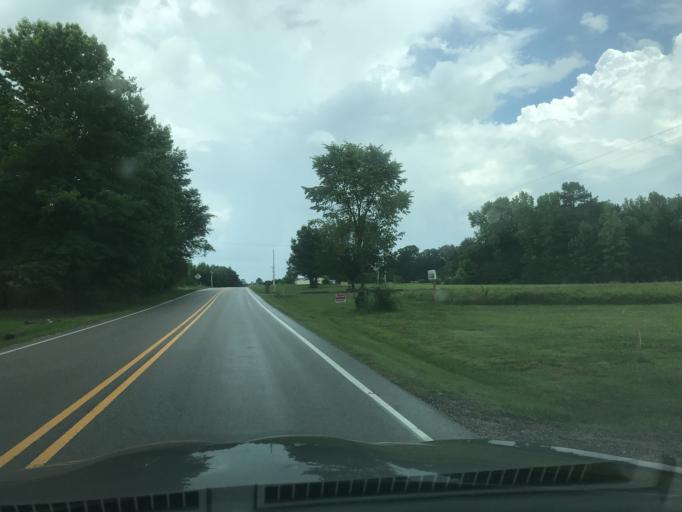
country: US
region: North Carolina
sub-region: Wake County
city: Knightdale
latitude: 35.8393
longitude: -78.5001
